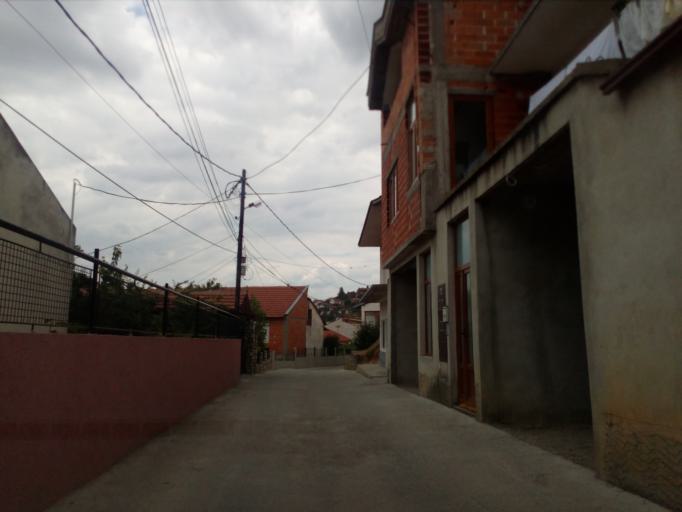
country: MK
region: Veles
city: Veles
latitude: 41.7089
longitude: 21.7596
